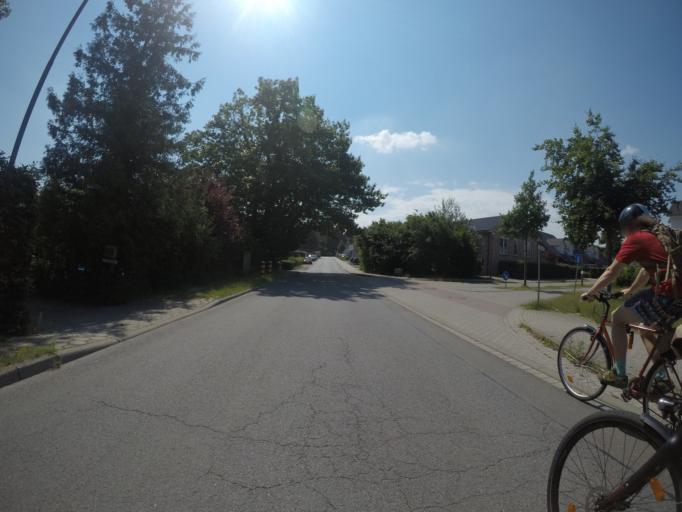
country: DE
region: Lower Saxony
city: Buchholz in der Nordheide
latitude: 53.3366
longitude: 9.8502
